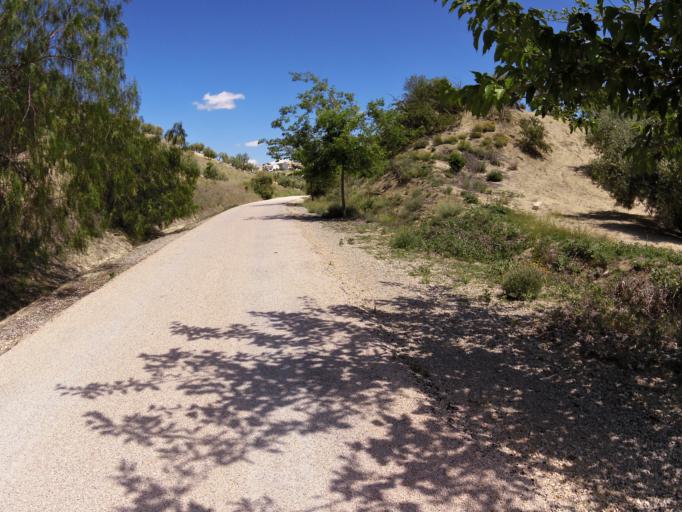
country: ES
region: Andalusia
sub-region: Provincia de Jaen
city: Torre del Campo
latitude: 37.7717
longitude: -3.9152
